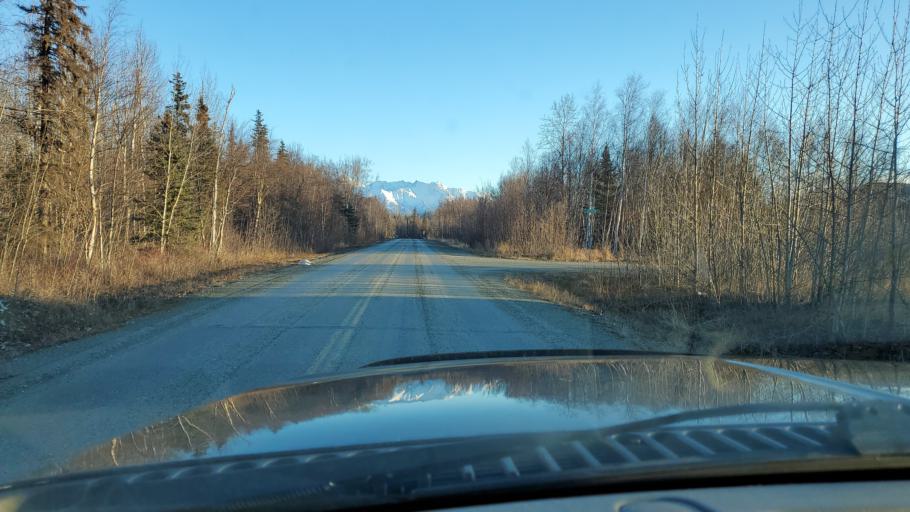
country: US
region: Alaska
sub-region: Matanuska-Susitna Borough
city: Gateway
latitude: 61.5885
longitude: -149.2554
